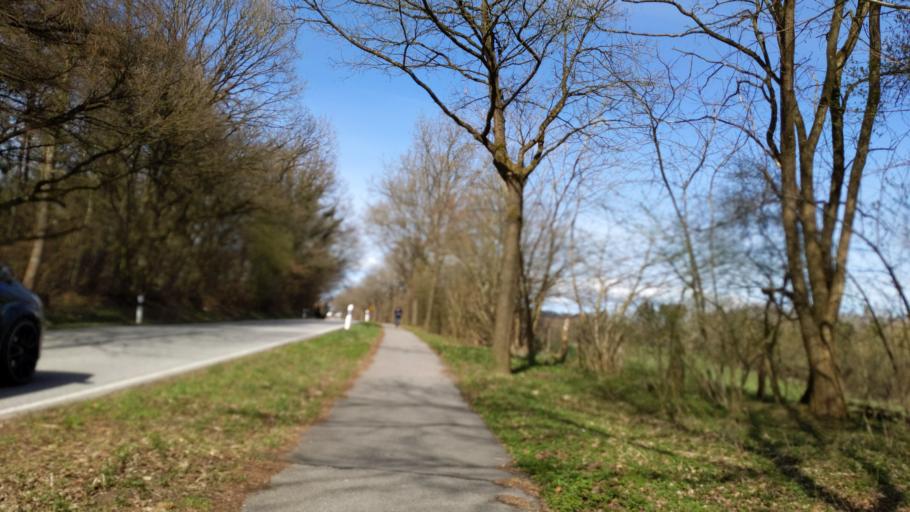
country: DE
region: Schleswig-Holstein
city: Ratekau
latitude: 53.9379
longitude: 10.7342
